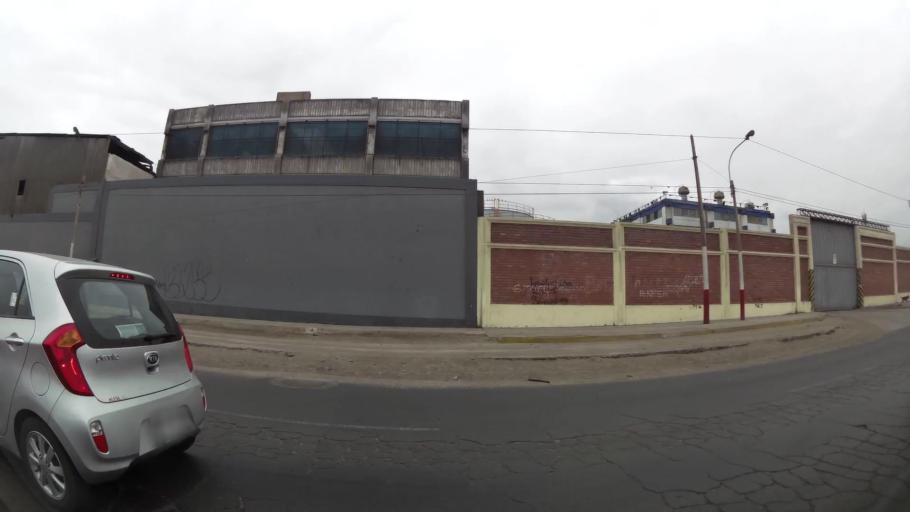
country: PE
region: Callao
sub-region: Callao
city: Callao
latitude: -12.0508
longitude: -77.1296
